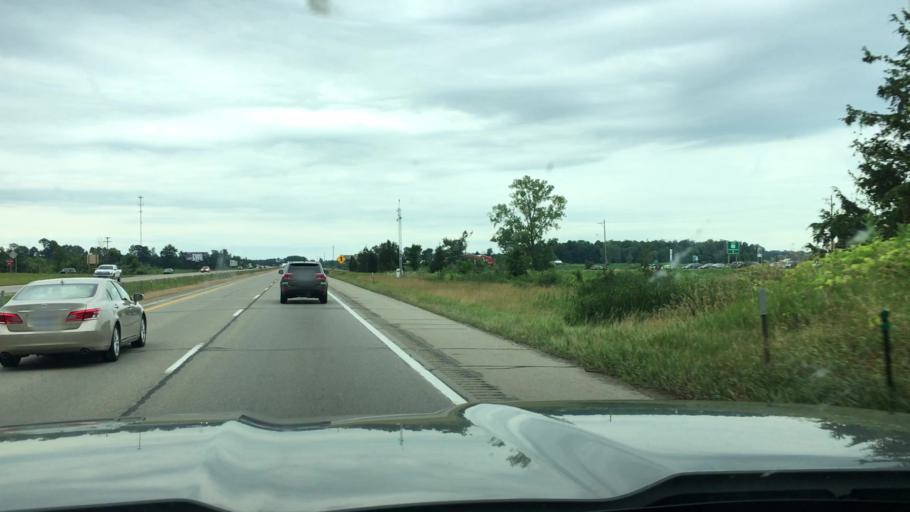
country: US
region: Michigan
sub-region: Allegan County
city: Wayland
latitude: 42.6303
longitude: -85.6625
